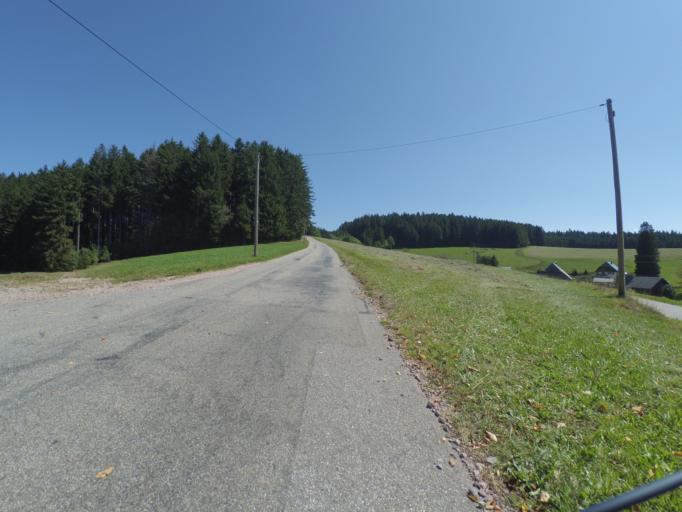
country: DE
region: Baden-Wuerttemberg
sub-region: Freiburg Region
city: Gutenbach
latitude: 48.0613
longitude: 8.1519
